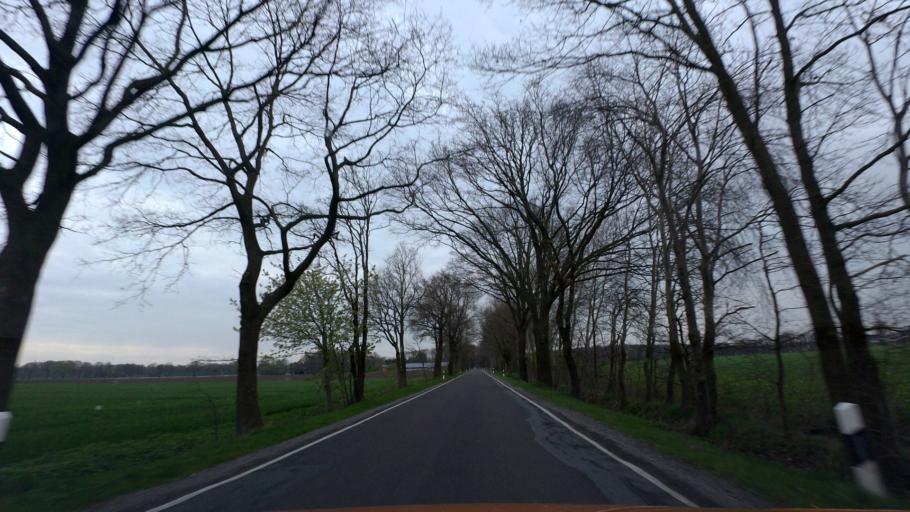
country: DE
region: Lower Saxony
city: Cloppenburg
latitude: 52.7709
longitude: 8.0193
